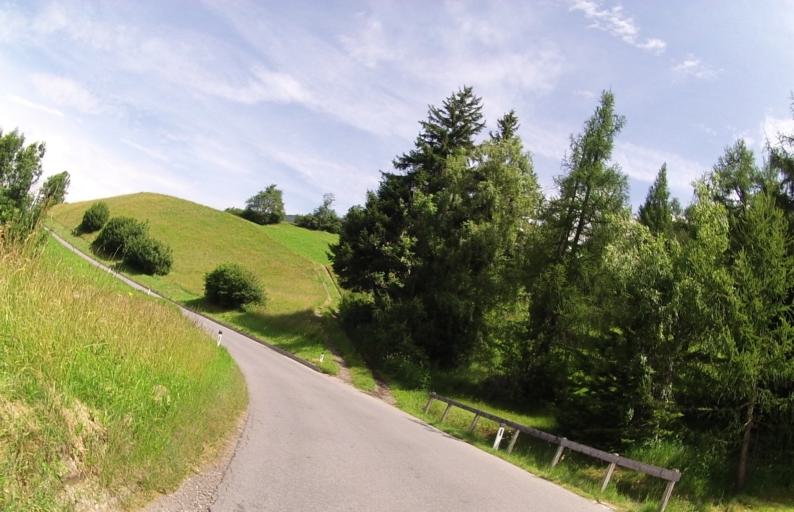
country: AT
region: Tyrol
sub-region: Politischer Bezirk Innsbruck Land
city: Pfons
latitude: 47.1537
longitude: 11.4548
